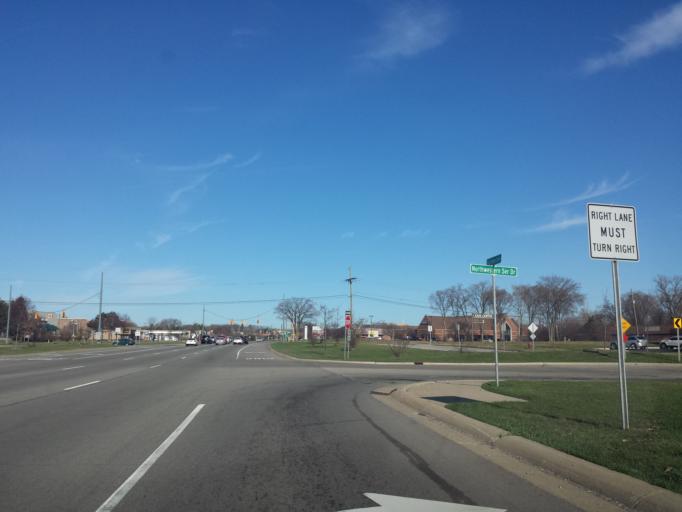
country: US
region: Michigan
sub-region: Oakland County
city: Franklin
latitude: 42.4977
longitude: -83.3005
